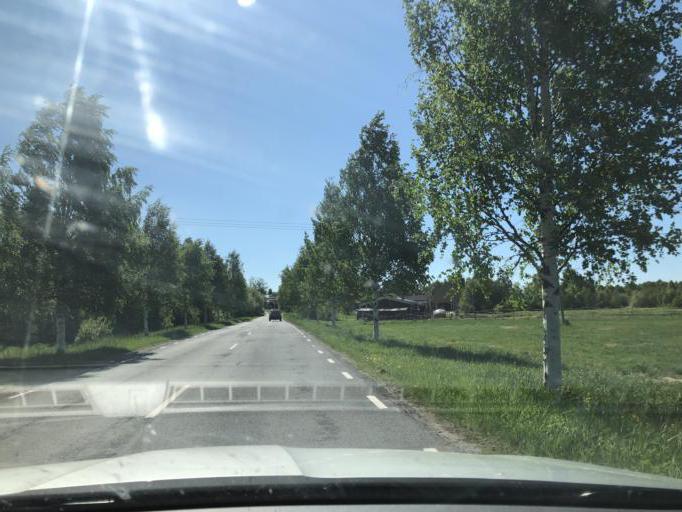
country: SE
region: Norrbotten
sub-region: Lulea Kommun
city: Gammelstad
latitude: 65.6495
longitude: 22.0203
